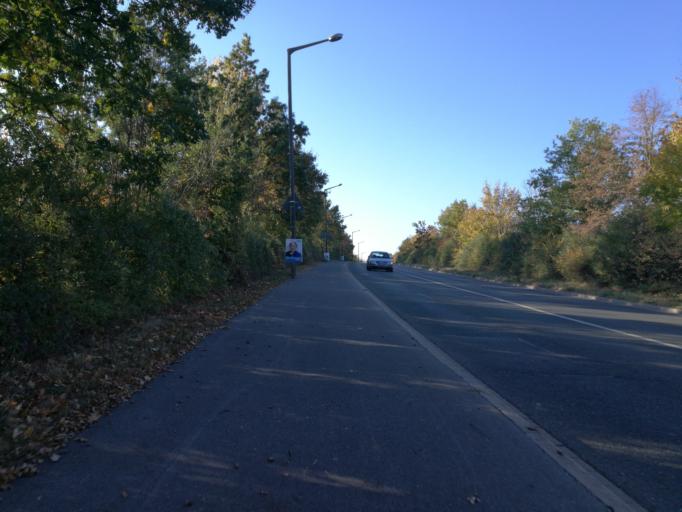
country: DE
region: Bavaria
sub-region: Regierungsbezirk Mittelfranken
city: Veitsbronn
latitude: 49.4956
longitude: 10.9177
